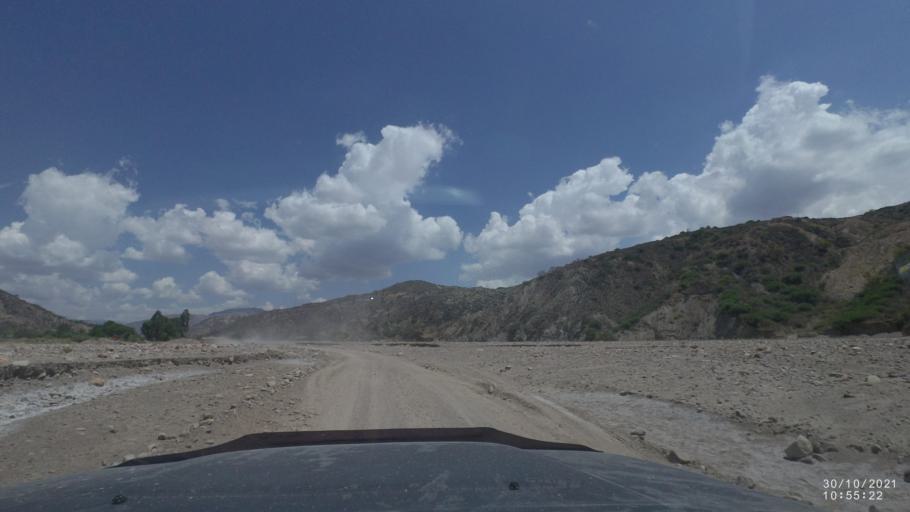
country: BO
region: Cochabamba
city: Sipe Sipe
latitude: -17.5423
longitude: -66.4890
